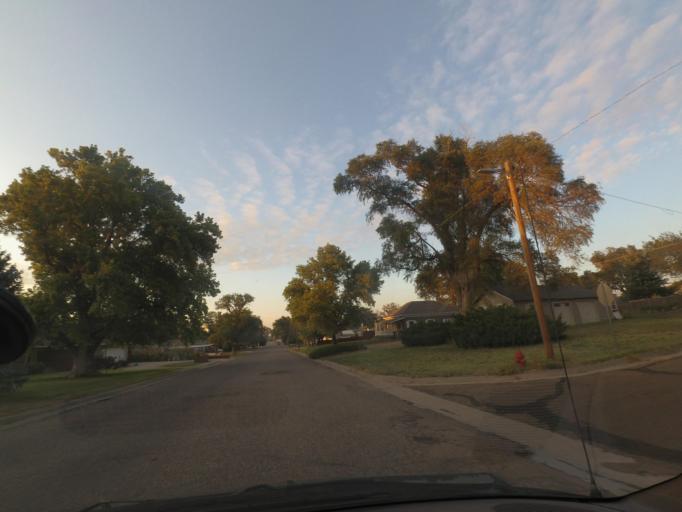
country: US
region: Kansas
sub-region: Cheyenne County
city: Saint Francis
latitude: 39.7691
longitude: -101.8053
